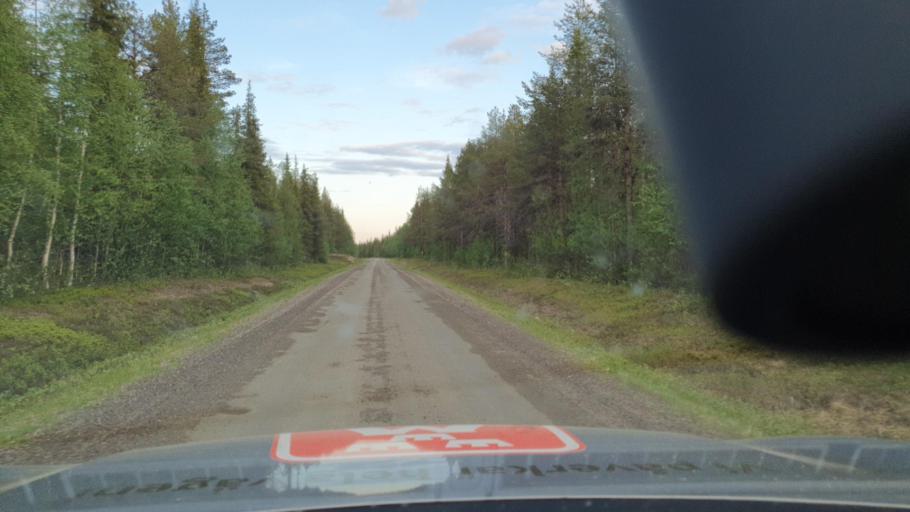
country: SE
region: Norrbotten
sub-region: Bodens Kommun
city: Boden
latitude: 66.5855
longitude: 21.3935
